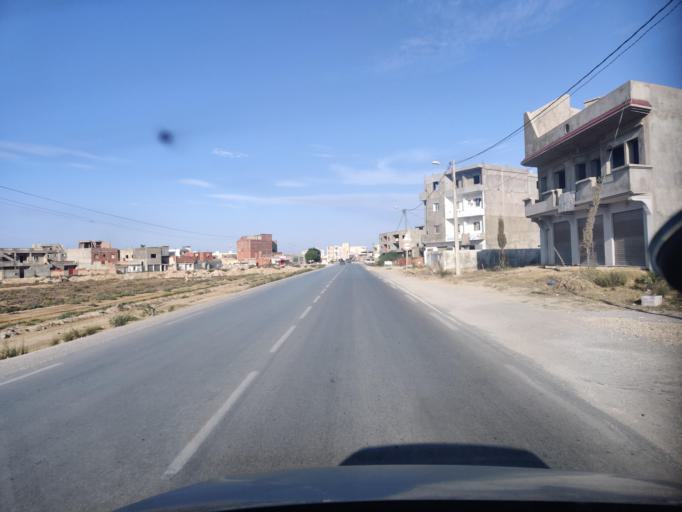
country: TN
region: Ariana
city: Ariana
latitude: 36.9555
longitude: 10.2257
